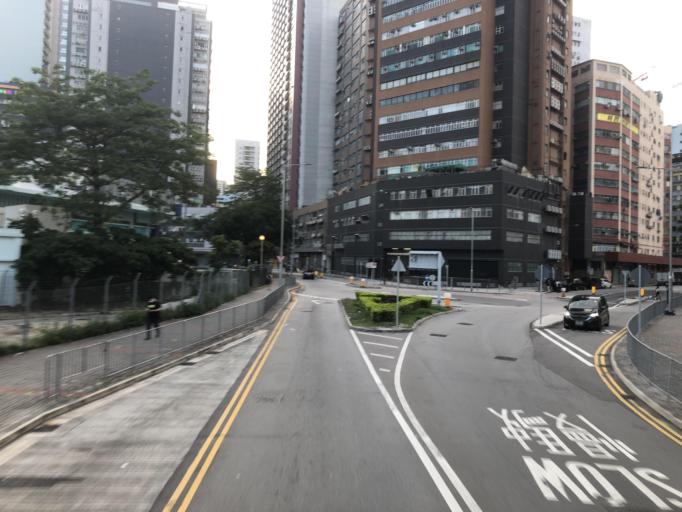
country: HK
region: Wong Tai Sin
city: Wong Tai Sin
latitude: 22.3358
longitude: 114.2012
